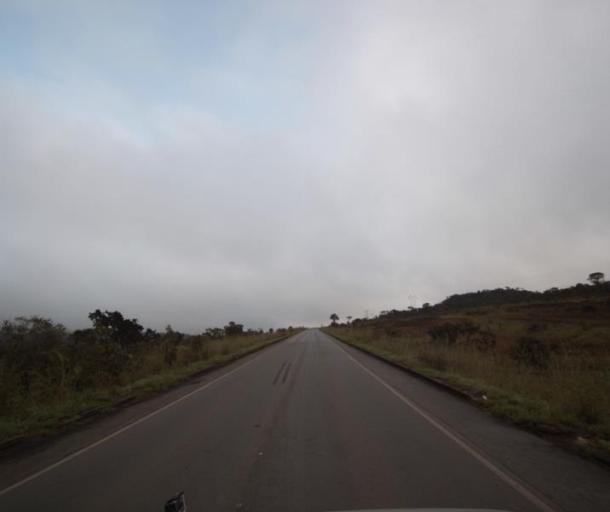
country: BR
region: Goias
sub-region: Pirenopolis
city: Pirenopolis
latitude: -15.8149
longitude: -48.7809
